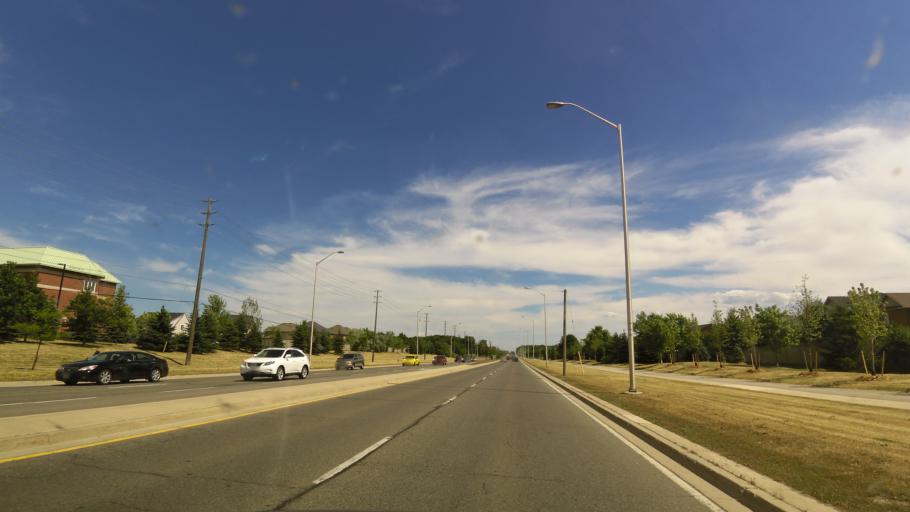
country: CA
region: Ontario
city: Burlington
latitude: 43.4267
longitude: -79.7644
